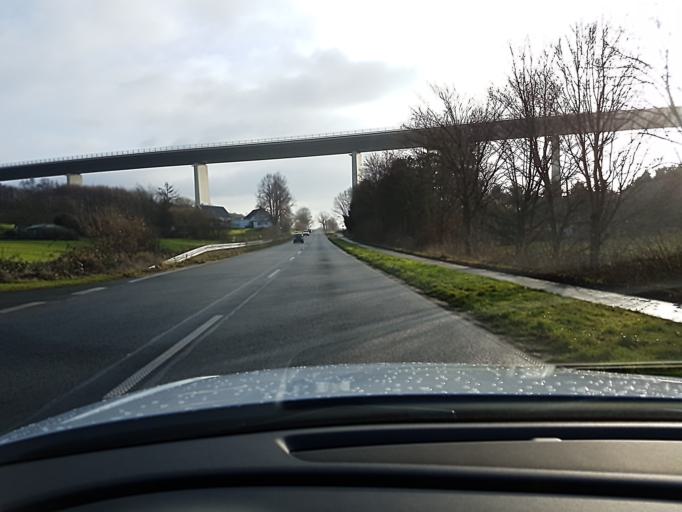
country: DE
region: North Rhine-Westphalia
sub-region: Regierungsbezirk Dusseldorf
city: Muelheim (Ruhr)
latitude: 51.3837
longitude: 6.9066
